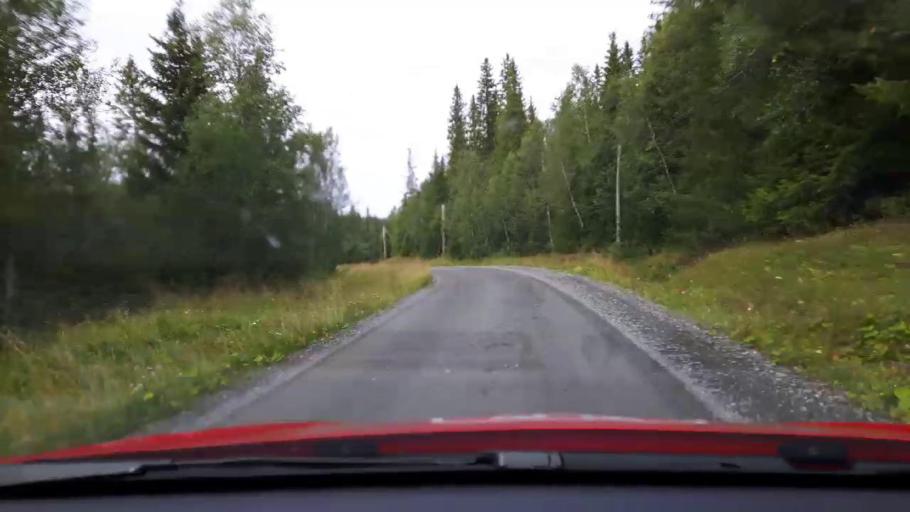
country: SE
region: Jaemtland
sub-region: Are Kommun
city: Are
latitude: 63.7678
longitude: 13.0930
